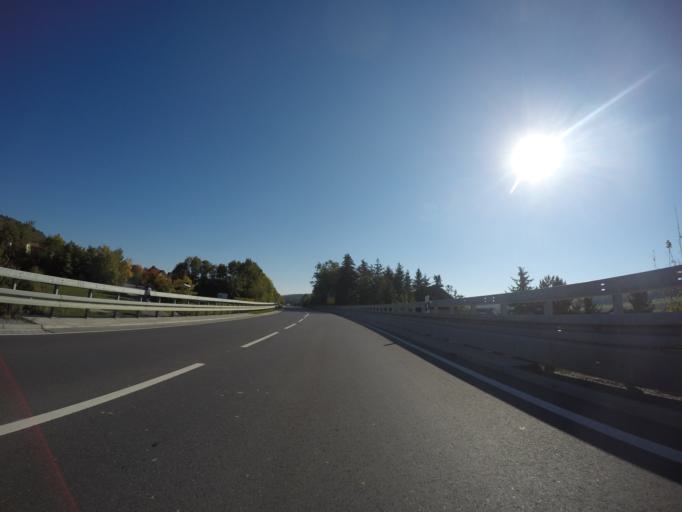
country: DE
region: Bavaria
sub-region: Regierungsbezirk Unterfranken
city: Uettingen
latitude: 49.7953
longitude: 9.7202
